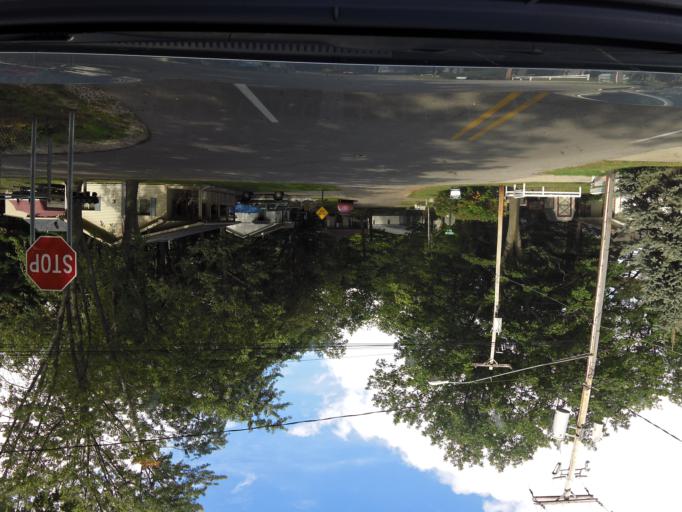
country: US
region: Michigan
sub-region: Roscommon County
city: Prudenville
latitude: 44.3025
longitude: -84.7032
